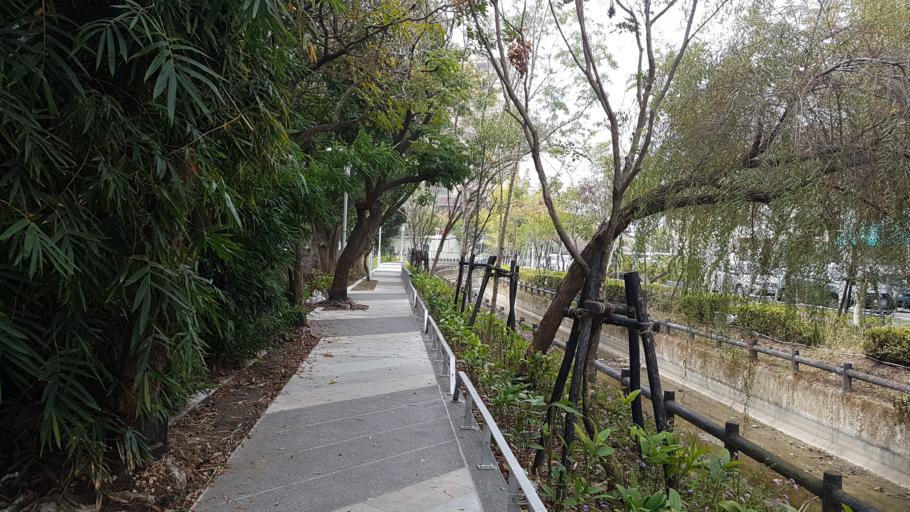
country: TW
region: Taiwan
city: Xinying
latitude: 23.3084
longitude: 120.3172
